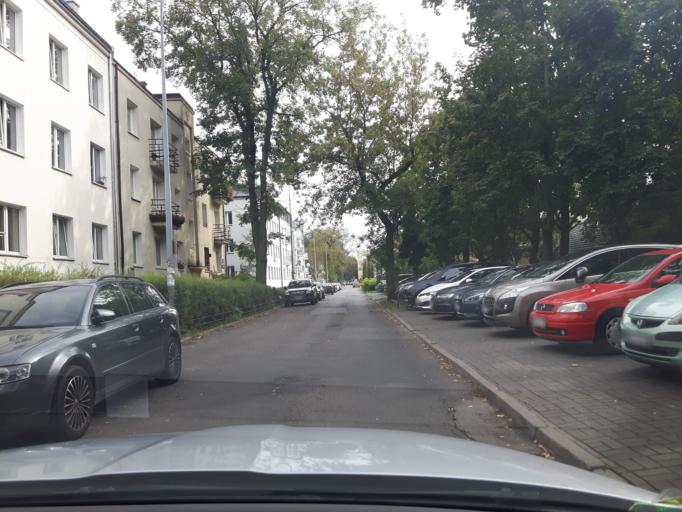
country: PL
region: Masovian Voivodeship
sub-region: Warszawa
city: Mokotow
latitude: 52.2025
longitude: 21.0286
